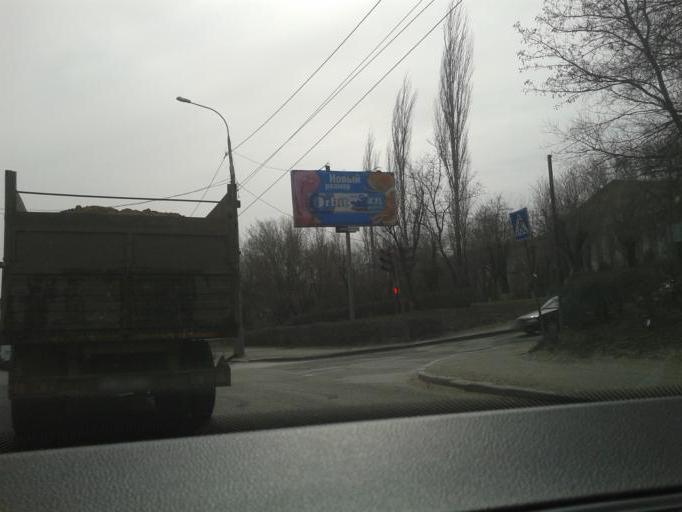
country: RU
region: Volgograd
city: Volgograd
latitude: 48.6756
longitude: 44.4439
